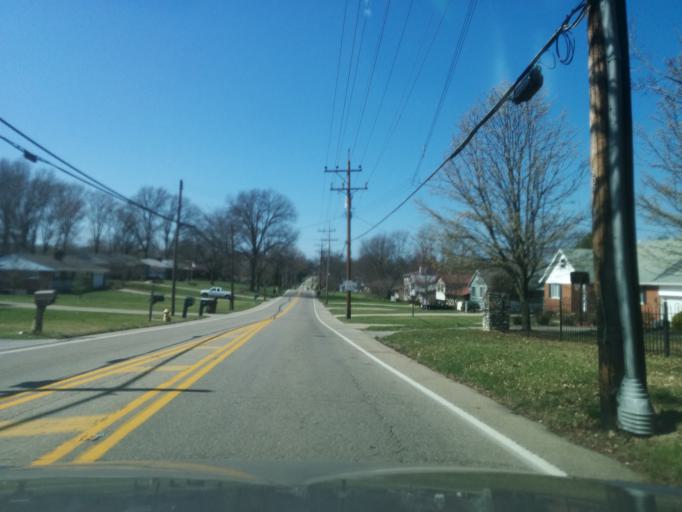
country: US
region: Ohio
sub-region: Hamilton County
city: Groesbeck
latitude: 39.2353
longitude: -84.5993
